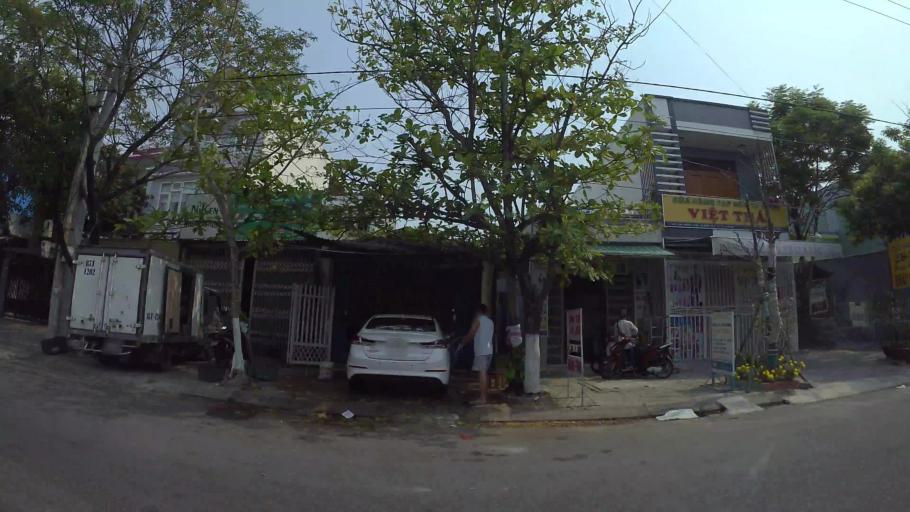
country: VN
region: Da Nang
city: Da Nang
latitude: 16.0951
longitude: 108.2299
